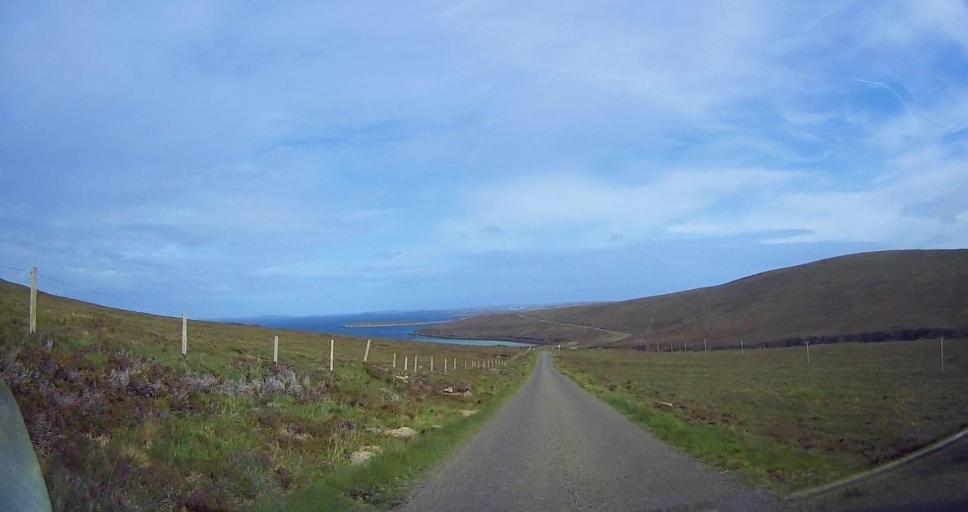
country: GB
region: Scotland
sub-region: Orkney Islands
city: Stromness
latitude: 58.8744
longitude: -3.2433
